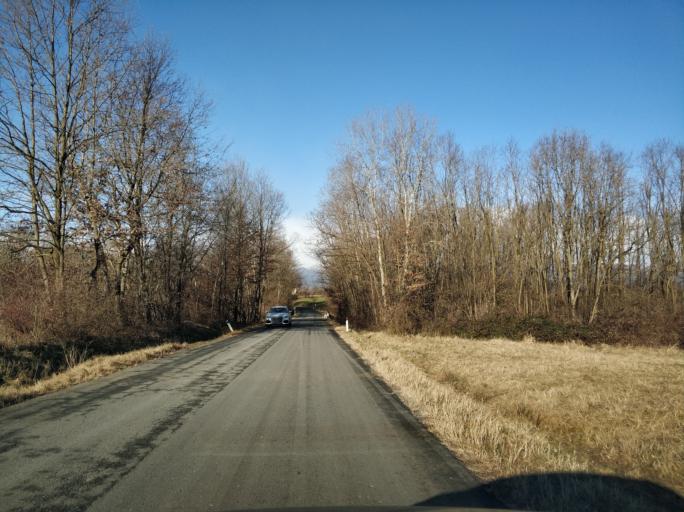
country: IT
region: Piedmont
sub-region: Provincia di Torino
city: Front
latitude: 45.2631
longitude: 7.6462
